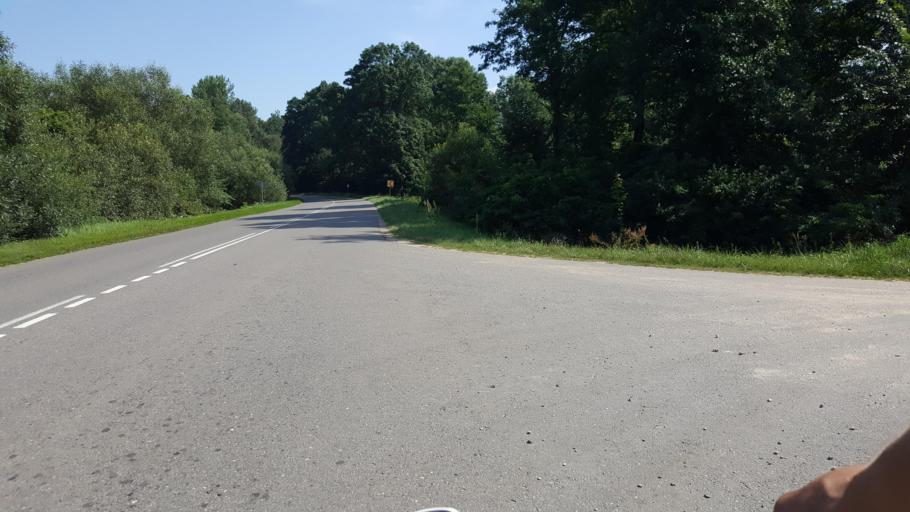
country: BY
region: Brest
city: Kamyanyuki
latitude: 52.4921
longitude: 23.6824
